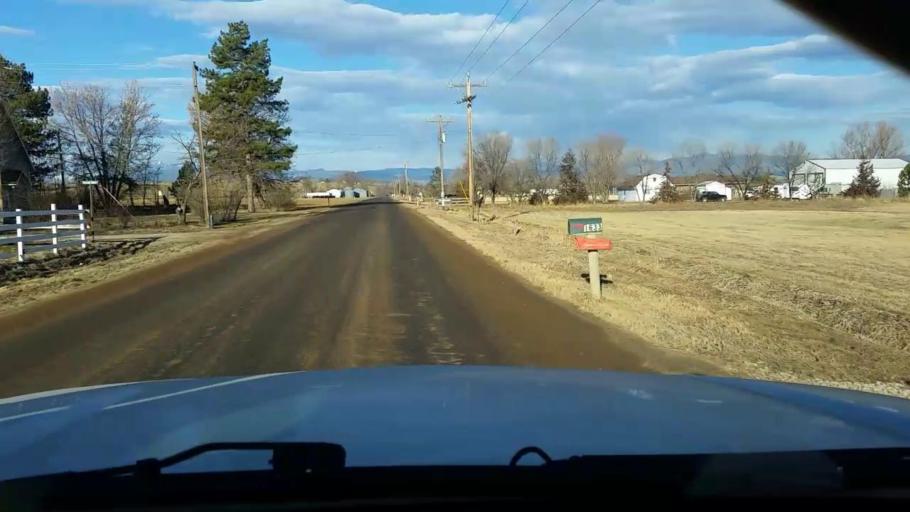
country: US
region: Colorado
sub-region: Larimer County
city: Campion
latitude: 40.3711
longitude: -105.0532
